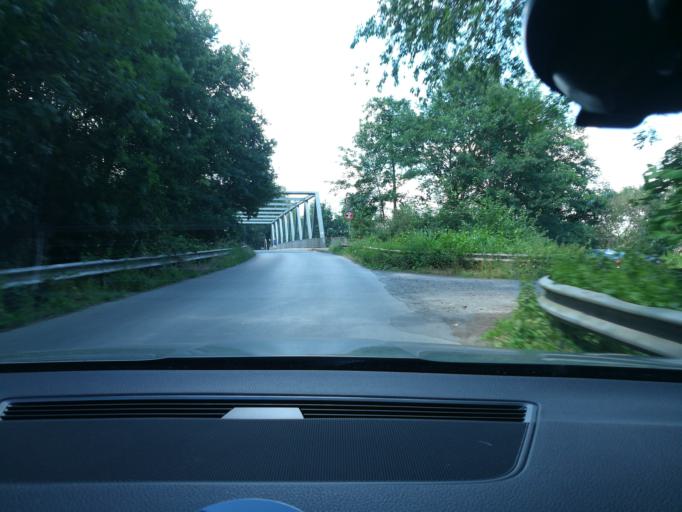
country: DE
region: North Rhine-Westphalia
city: Lubbecke
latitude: 52.3338
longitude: 8.6353
